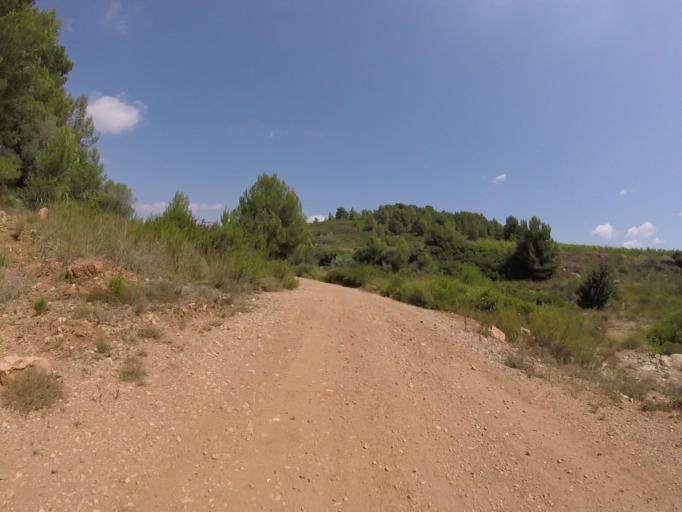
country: ES
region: Valencia
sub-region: Provincia de Castello
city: Torreblanca
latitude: 40.2156
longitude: 0.1479
